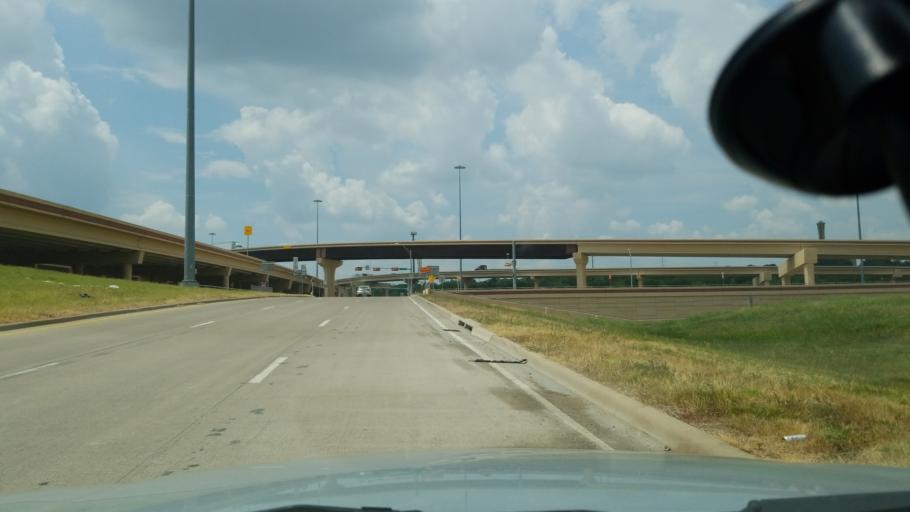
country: US
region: Texas
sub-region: Dallas County
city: Irving
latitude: 32.8478
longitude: -96.9110
